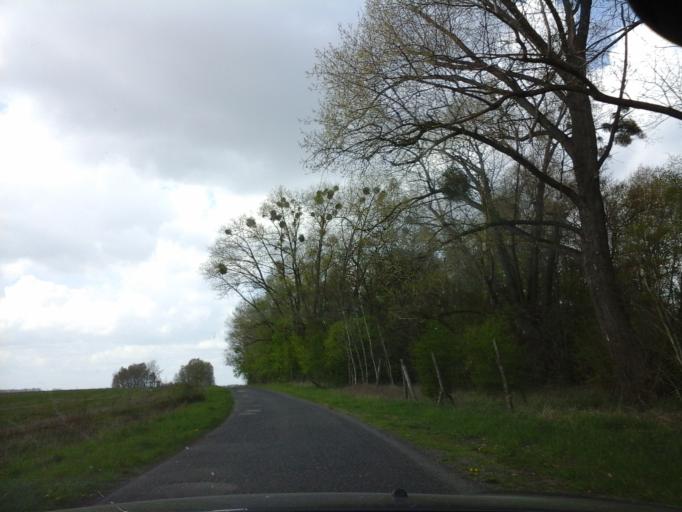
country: PL
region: West Pomeranian Voivodeship
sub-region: Powiat stargardzki
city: Dobrzany
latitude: 53.3276
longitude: 15.4279
